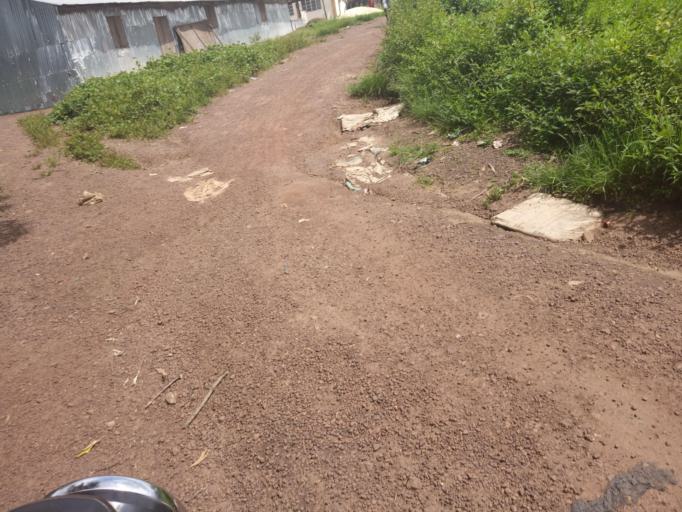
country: SL
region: Northern Province
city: Kamakwie
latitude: 9.4952
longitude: -12.2447
